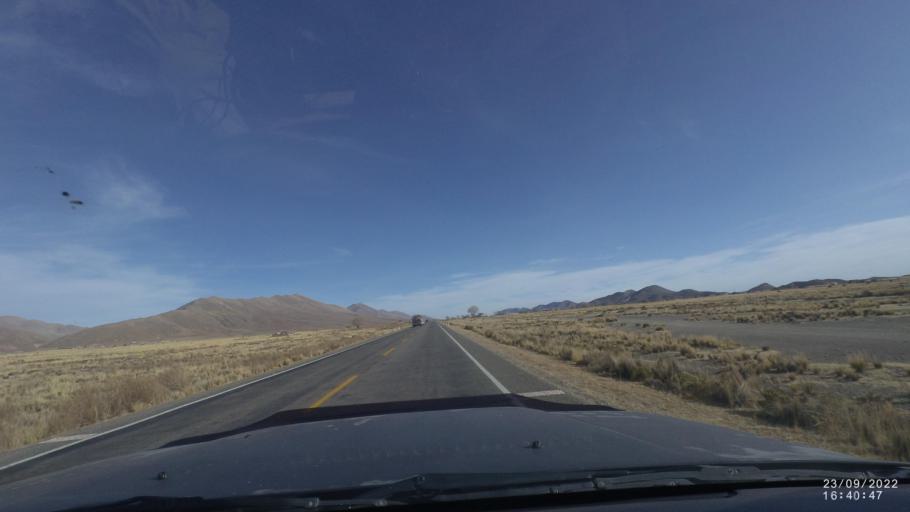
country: BO
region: Oruro
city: Poopo
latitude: -18.2821
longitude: -66.9950
